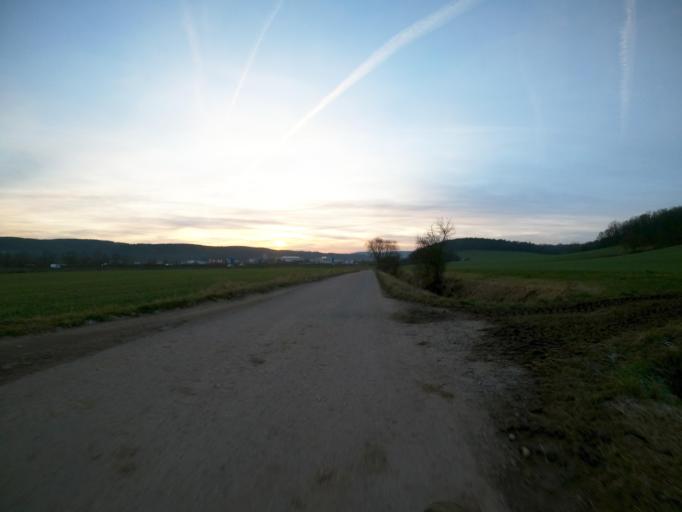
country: DE
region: Thuringia
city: Laasdorf
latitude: 50.8791
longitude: 11.6746
